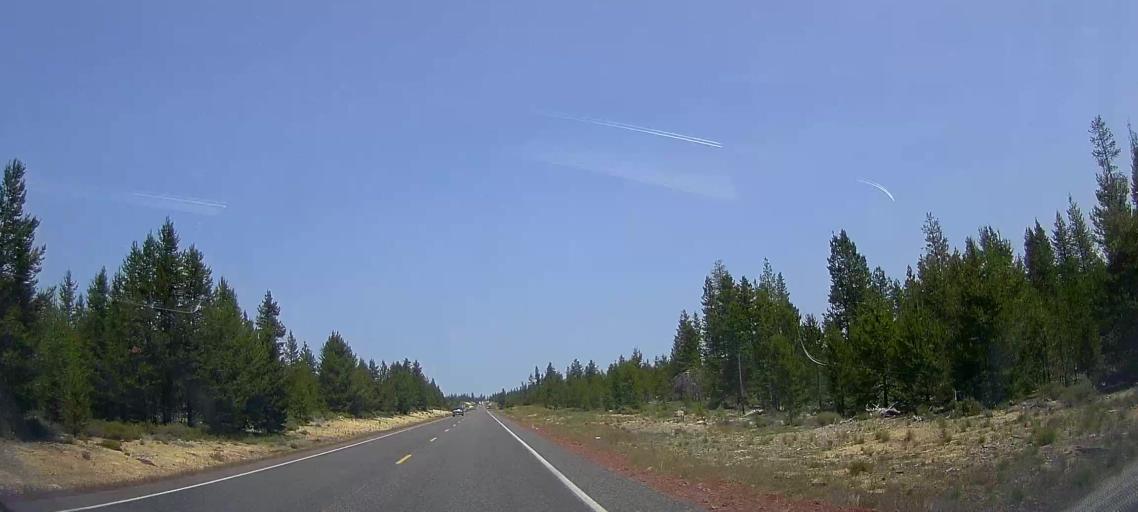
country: US
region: Oregon
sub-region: Deschutes County
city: La Pine
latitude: 43.3937
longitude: -121.7271
